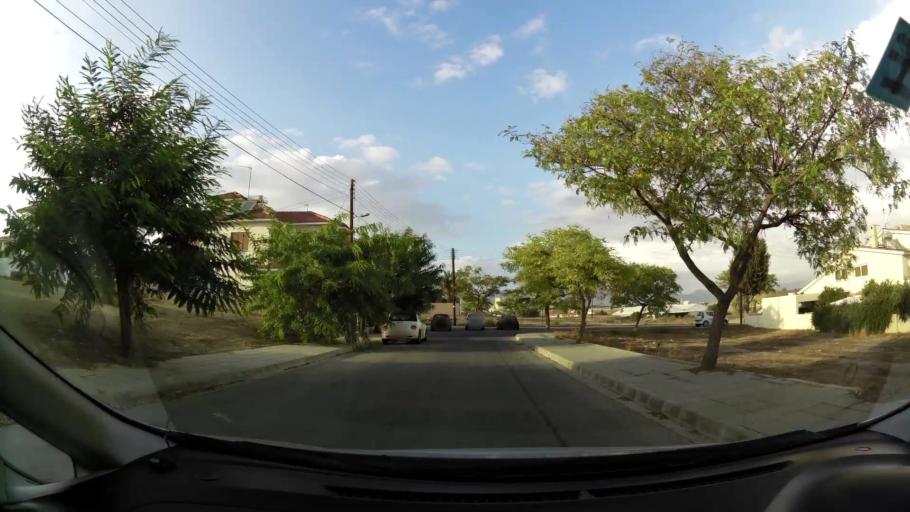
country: CY
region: Lefkosia
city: Nicosia
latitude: 35.1676
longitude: 33.3962
